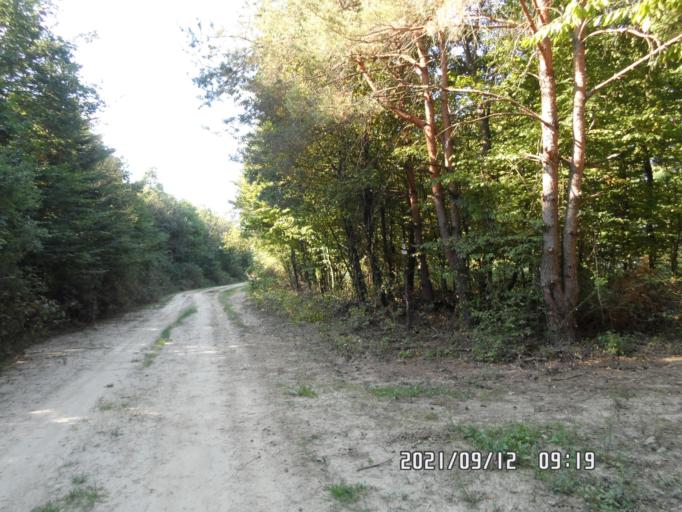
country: HU
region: Zala
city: Zalalovo
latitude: 46.8042
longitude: 16.6561
